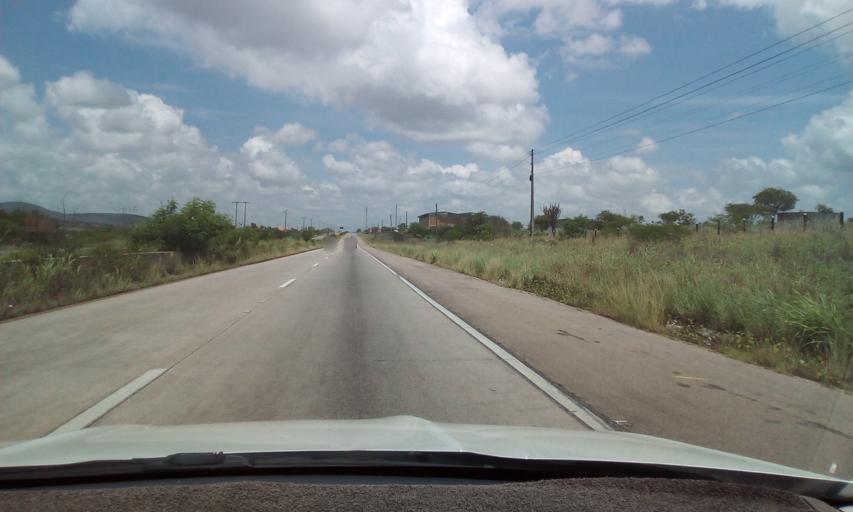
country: BR
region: Pernambuco
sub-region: Gravata
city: Gravata
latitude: -8.2152
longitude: -35.6377
